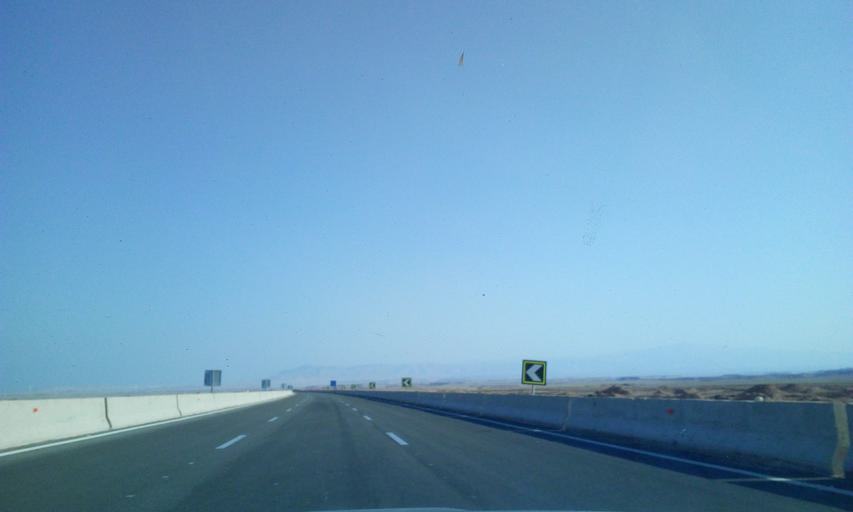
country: EG
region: As Suways
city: Ain Sukhna
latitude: 29.1979
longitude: 32.4956
